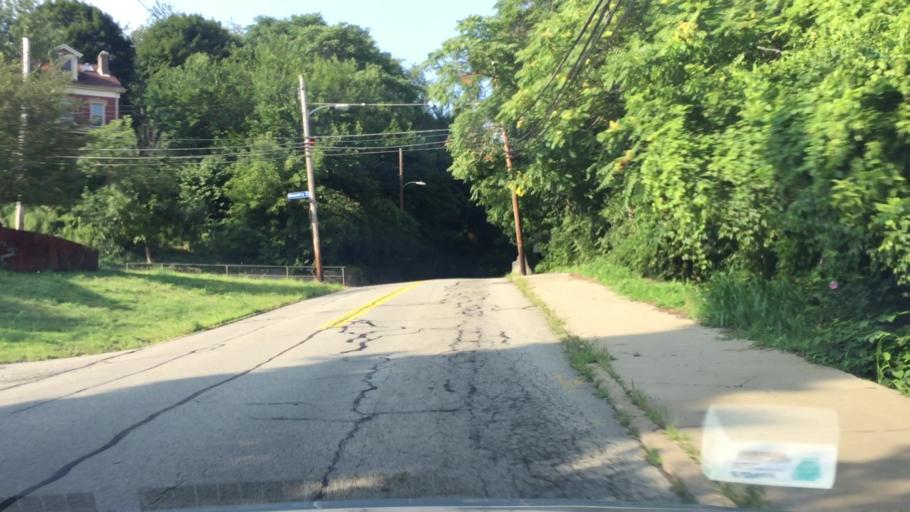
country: US
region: Pennsylvania
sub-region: Allegheny County
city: Mount Oliver
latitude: 40.4241
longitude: -79.9864
